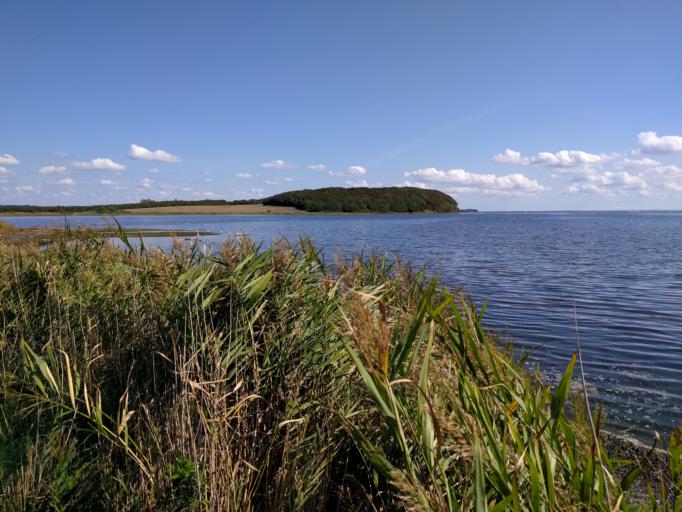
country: DK
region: Central Jutland
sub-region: Skive Kommune
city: Hojslev
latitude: 56.6658
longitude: 9.0952
